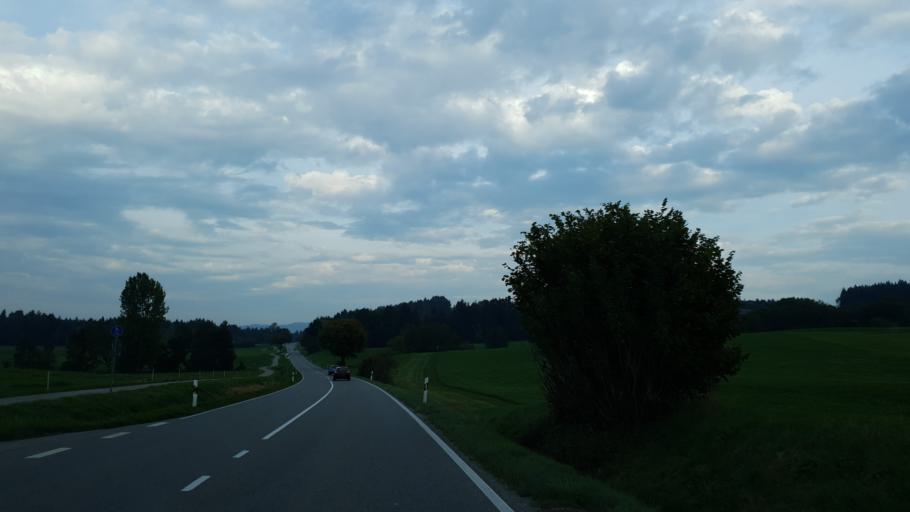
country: DE
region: Bavaria
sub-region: Swabia
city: Gestratz
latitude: 47.6752
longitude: 9.9636
